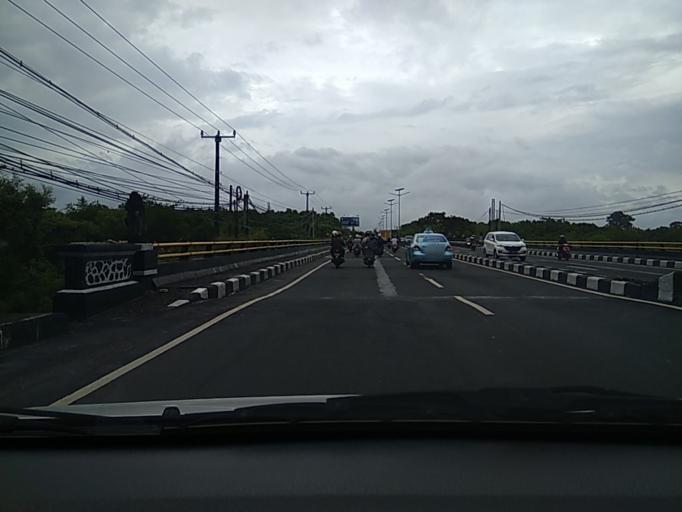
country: ID
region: Bali
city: Kelanabian
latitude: -8.7752
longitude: 115.1777
